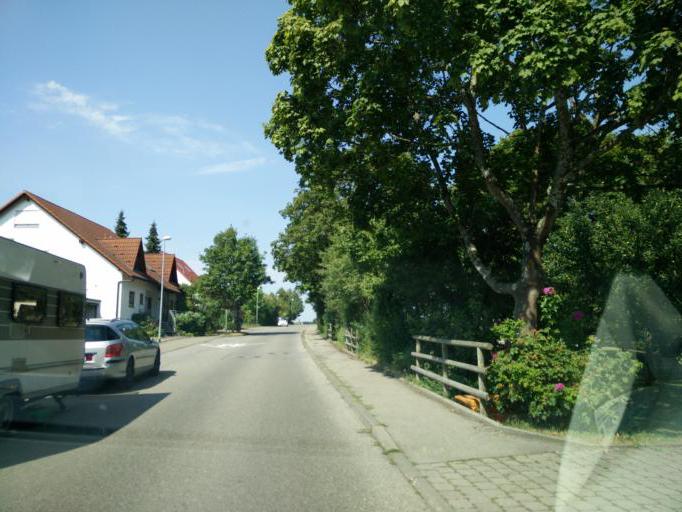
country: DE
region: Baden-Wuerttemberg
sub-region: Tuebingen Region
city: Kusterdingen
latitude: 48.5523
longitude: 9.1074
